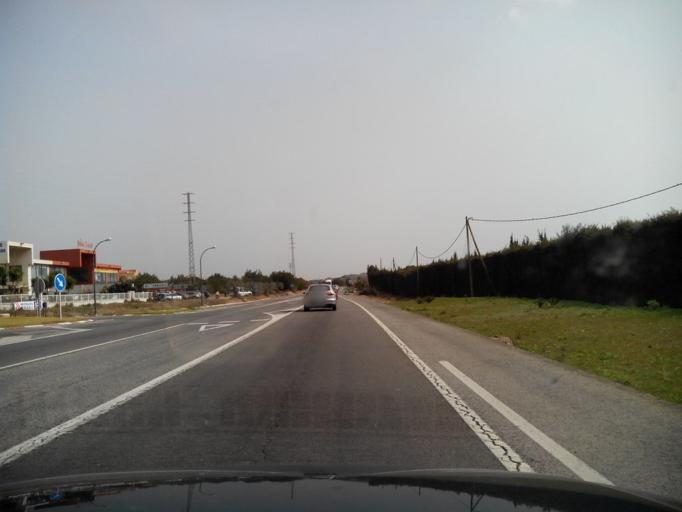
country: ES
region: Catalonia
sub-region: Provincia de Tarragona
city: Creixell
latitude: 41.1621
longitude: 1.4394
